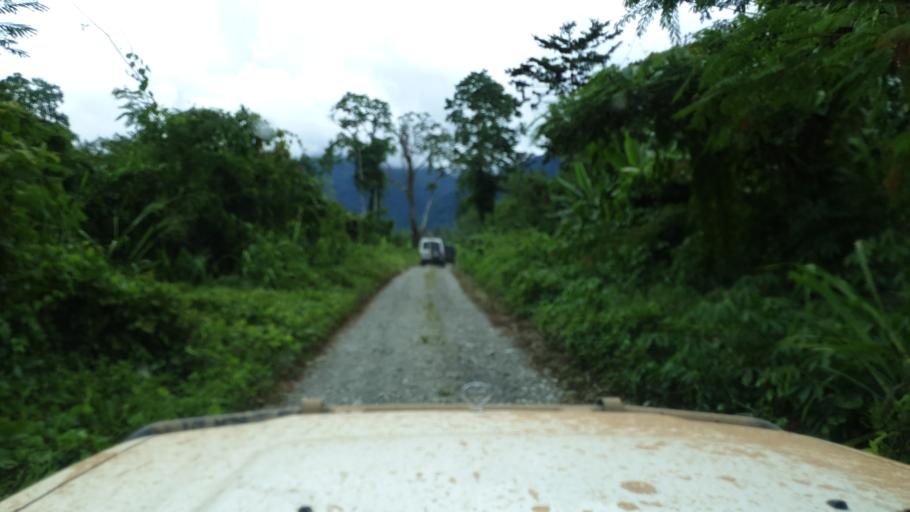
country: PG
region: Northern Province
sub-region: Sohe
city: Kokoda
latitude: -8.9368
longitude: 147.8676
